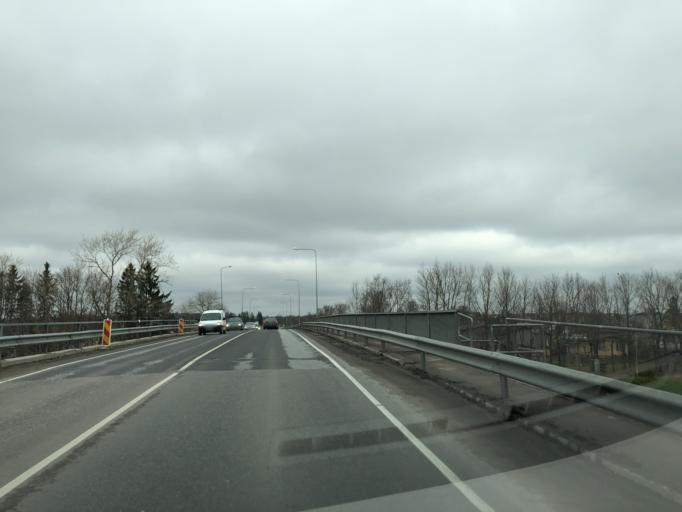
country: EE
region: Laeaene-Virumaa
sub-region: Rakvere linn
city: Rakvere
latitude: 59.3540
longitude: 26.3372
